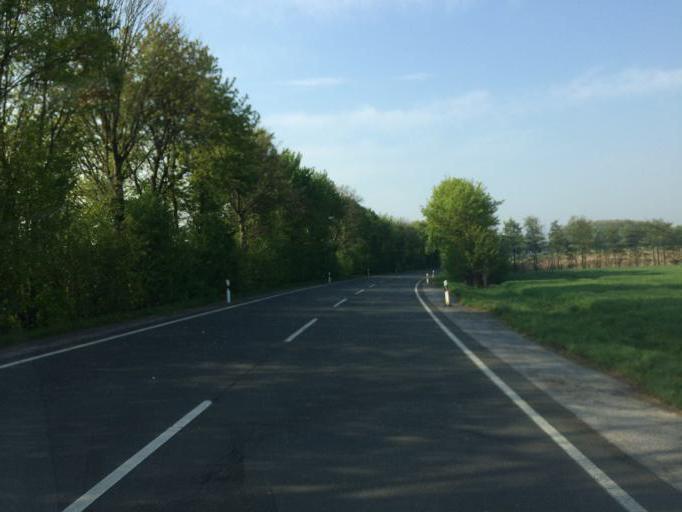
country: DE
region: North Rhine-Westphalia
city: Witten
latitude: 51.4645
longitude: 7.3910
